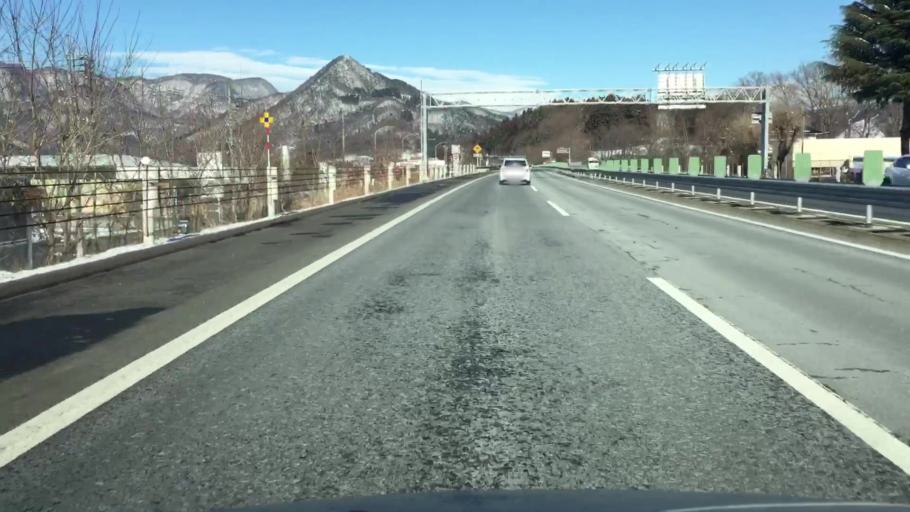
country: JP
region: Gunma
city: Numata
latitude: 36.6600
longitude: 139.0682
